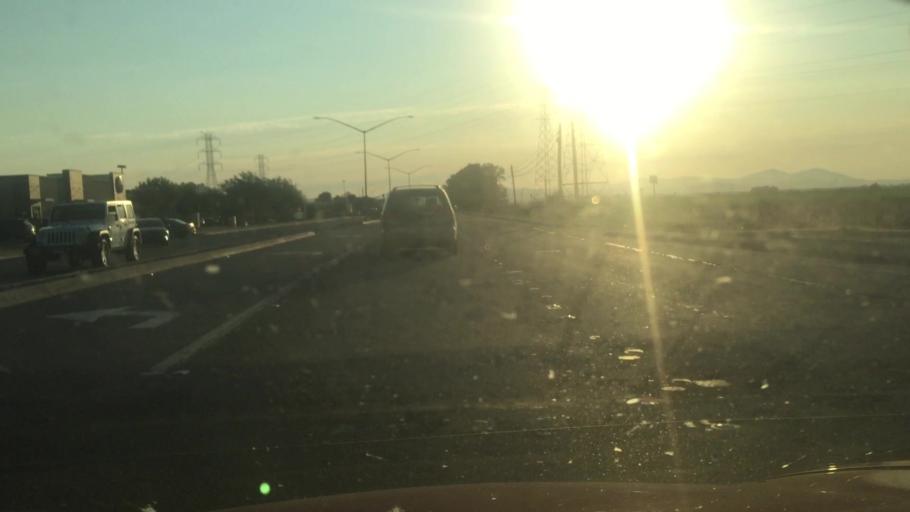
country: US
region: California
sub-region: San Joaquin County
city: Tracy
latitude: 37.7541
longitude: -121.4686
